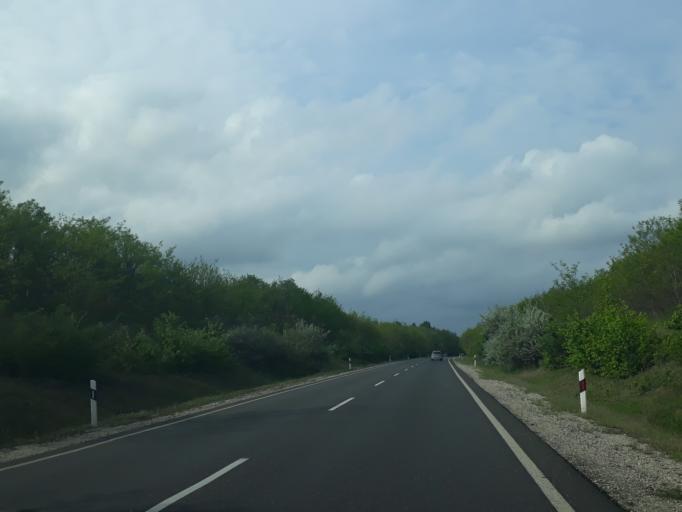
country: HU
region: Szabolcs-Szatmar-Bereg
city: Nyirtass
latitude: 48.0978
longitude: 21.9872
